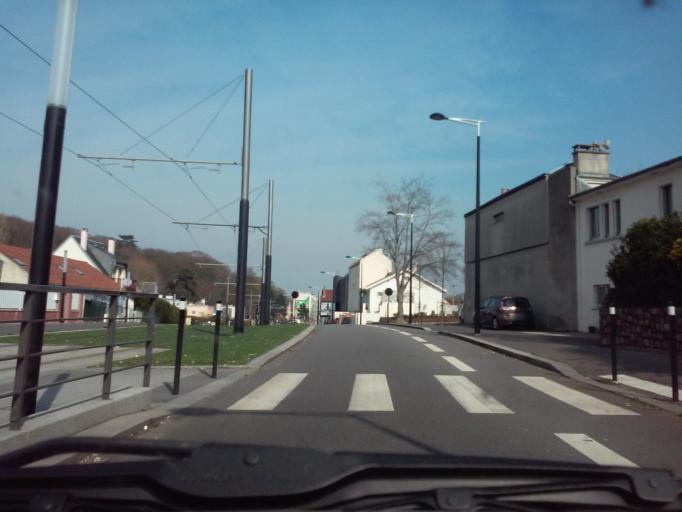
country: FR
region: Haute-Normandie
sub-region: Departement de la Seine-Maritime
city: Fontaine-la-Mallet
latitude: 49.5086
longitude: 0.1383
